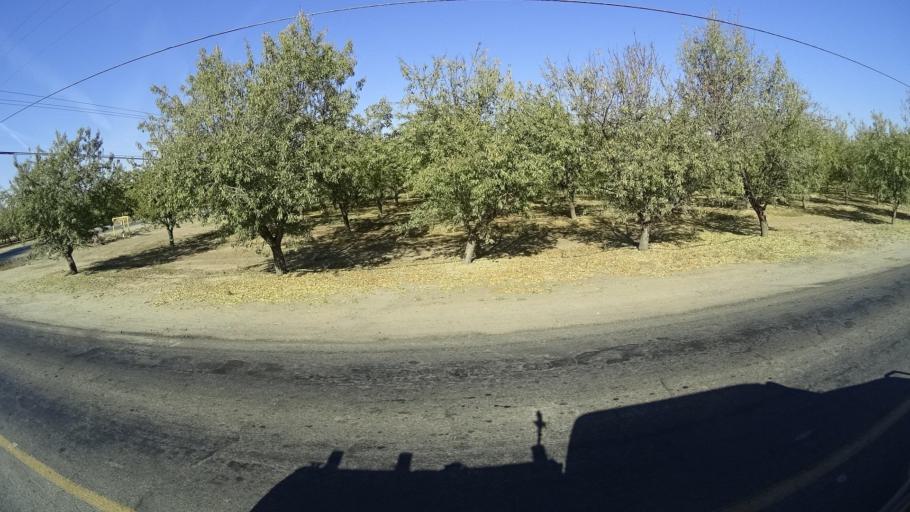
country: US
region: California
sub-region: Kern County
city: McFarland
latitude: 35.6895
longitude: -119.2230
